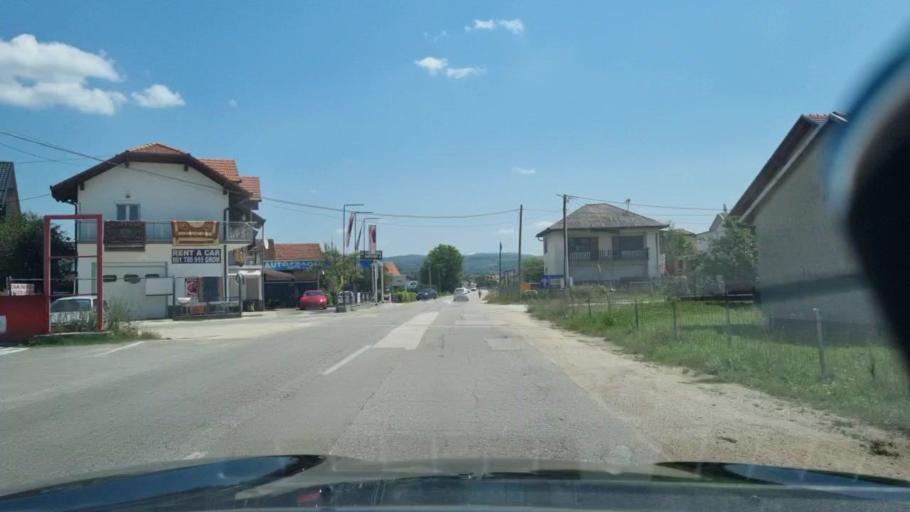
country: BA
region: Federation of Bosnia and Herzegovina
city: Sanski Most
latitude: 44.7712
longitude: 16.6595
